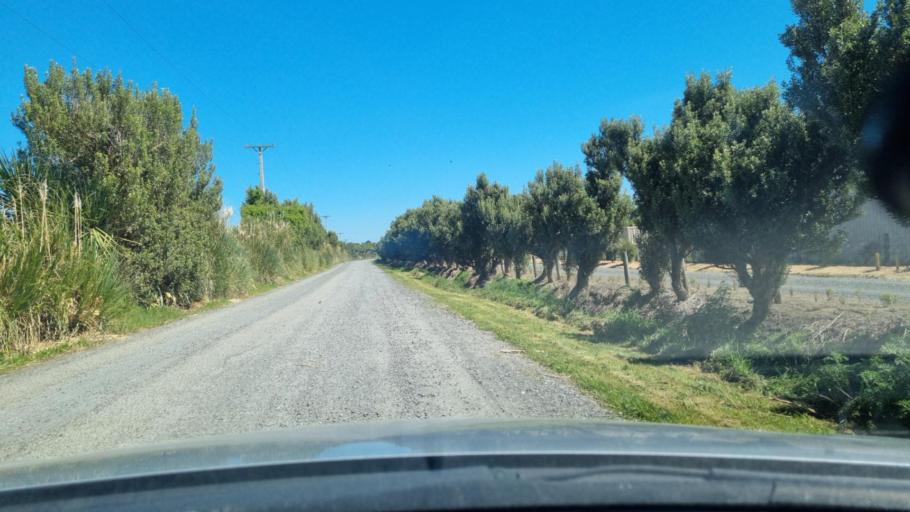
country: NZ
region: Southland
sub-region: Invercargill City
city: Invercargill
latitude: -46.4445
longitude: 168.2781
